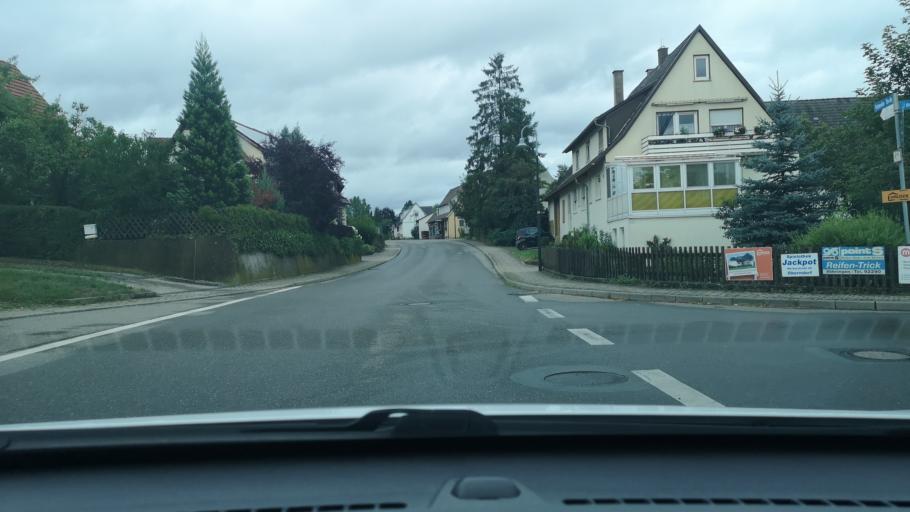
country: DE
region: Baden-Wuerttemberg
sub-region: Freiburg Region
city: Vohringen
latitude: 48.3328
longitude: 8.6571
